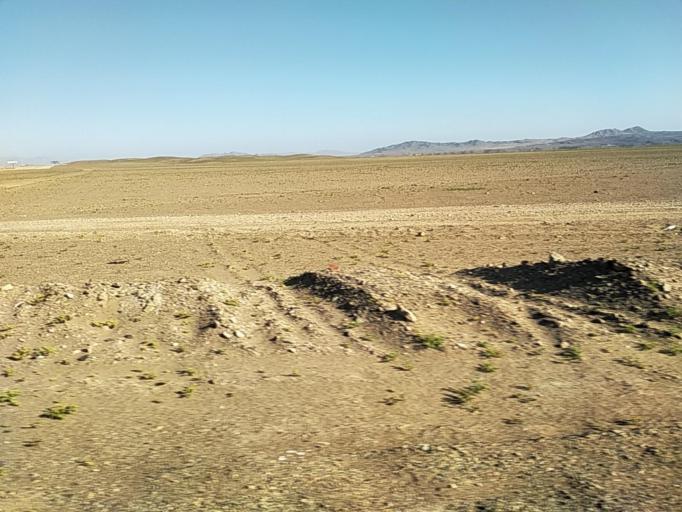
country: CL
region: Atacama
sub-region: Provincia de Copiapo
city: Copiapo
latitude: -27.3196
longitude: -70.7385
